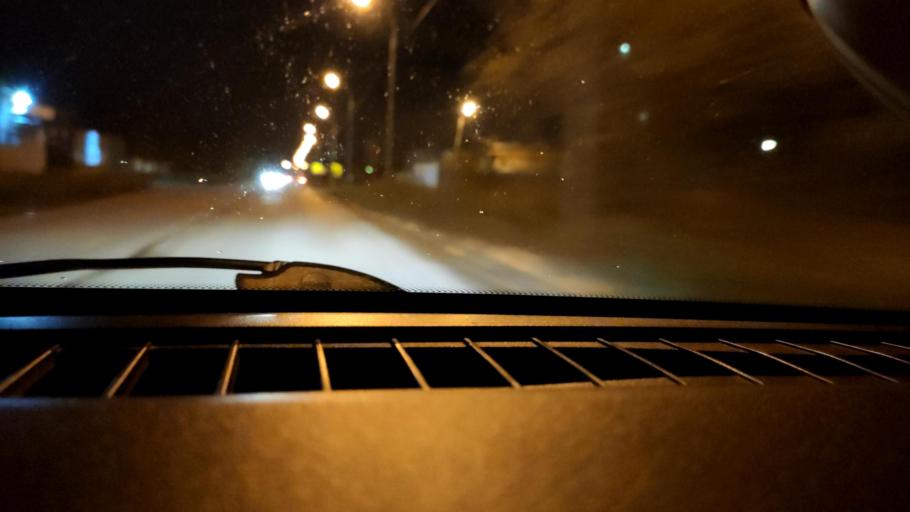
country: RU
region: Samara
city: Petra-Dubrava
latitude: 53.2388
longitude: 50.2960
